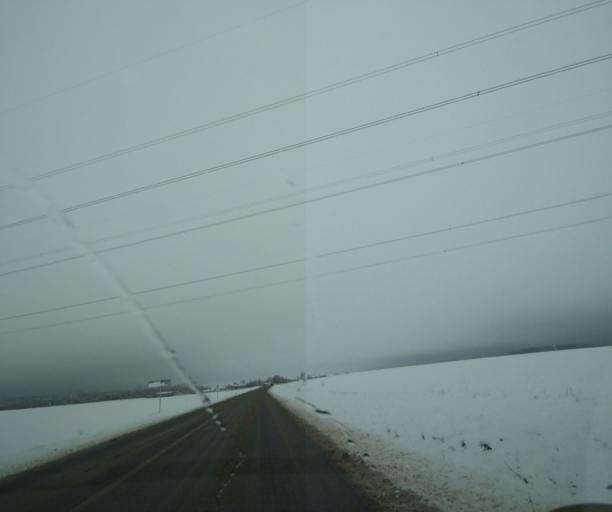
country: FR
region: Champagne-Ardenne
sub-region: Departement de la Haute-Marne
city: Wassy
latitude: 48.5179
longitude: 4.9348
